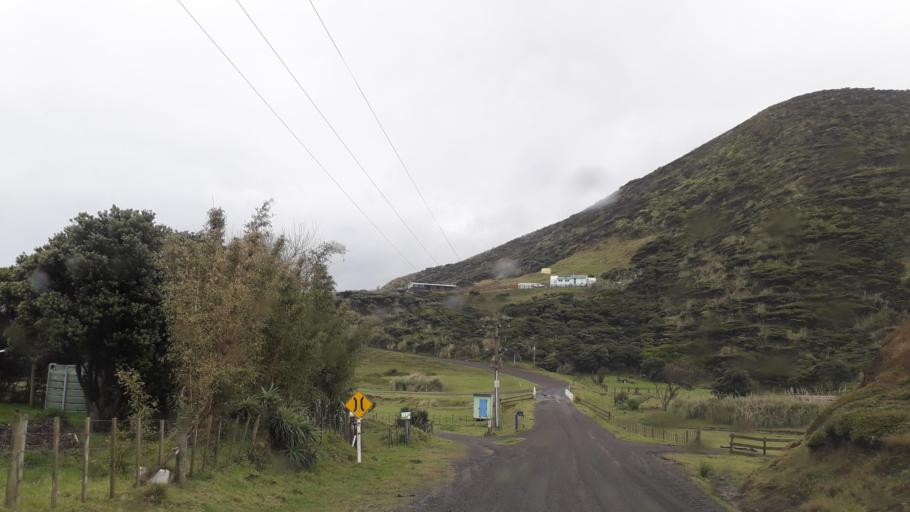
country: NZ
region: Northland
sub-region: Far North District
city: Ahipara
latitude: -35.4346
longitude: 173.2829
